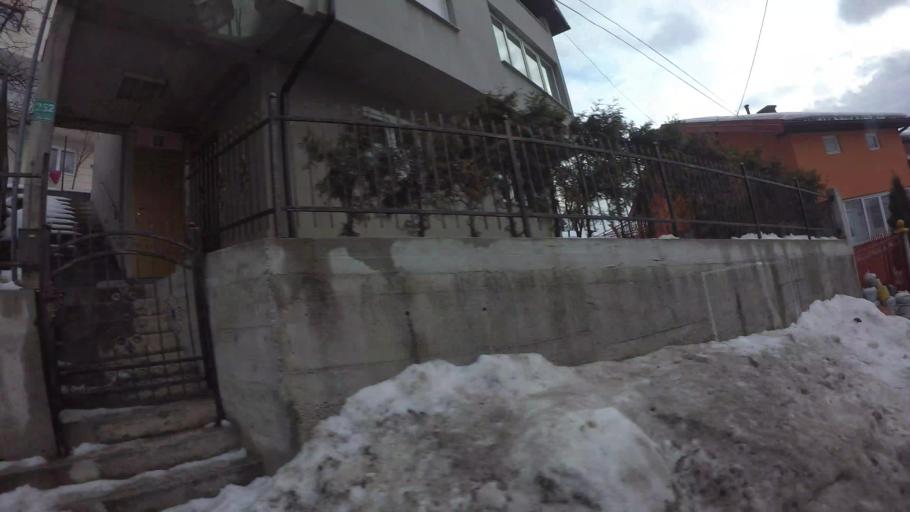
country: BA
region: Federation of Bosnia and Herzegovina
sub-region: Kanton Sarajevo
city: Sarajevo
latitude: 43.8614
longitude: 18.3514
